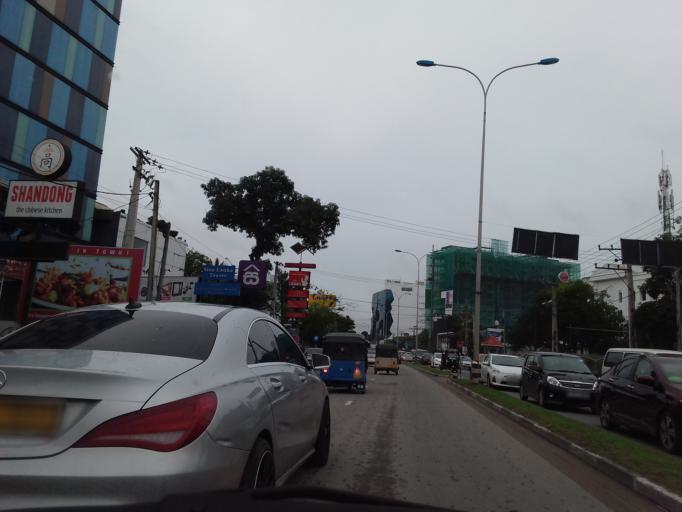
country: LK
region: Western
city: Pita Kotte
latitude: 6.9079
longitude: 79.8993
